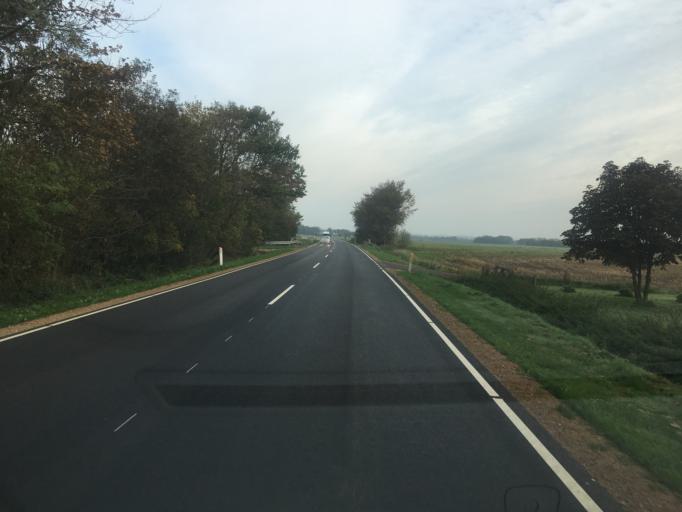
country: DK
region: South Denmark
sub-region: Tonder Kommune
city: Logumkloster
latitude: 55.0966
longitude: 9.0241
